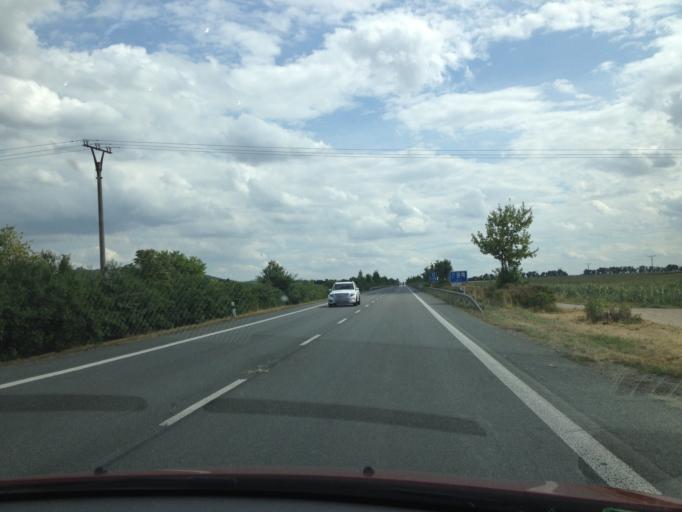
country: CZ
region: South Moravian
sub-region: Okres Breclav
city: Dolni Dunajovice
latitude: 48.8773
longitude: 16.6041
